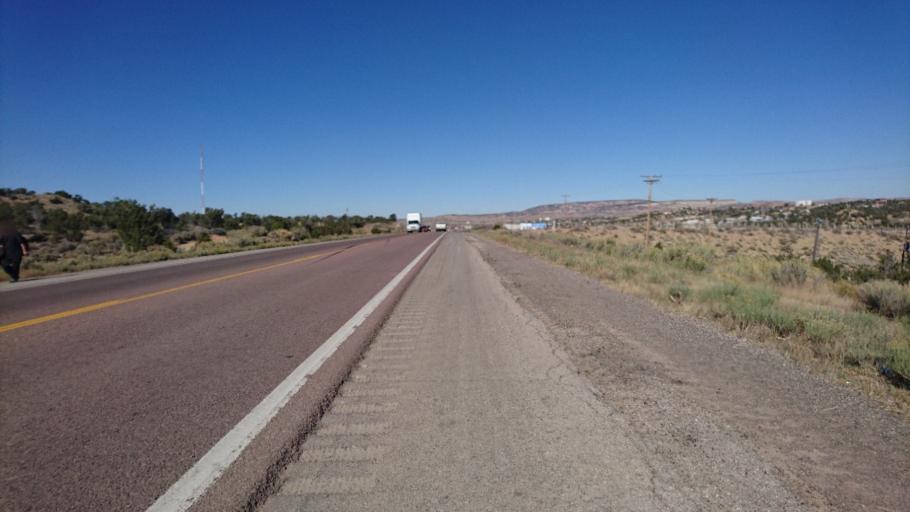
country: US
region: New Mexico
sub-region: McKinley County
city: Gallup
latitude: 35.4906
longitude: -108.7410
